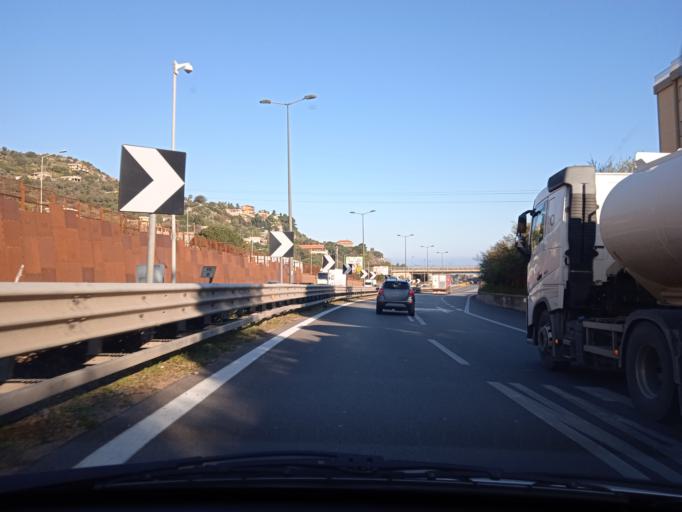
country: IT
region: Sicily
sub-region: Palermo
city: Isola delle Femmine
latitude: 38.1880
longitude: 13.2841
